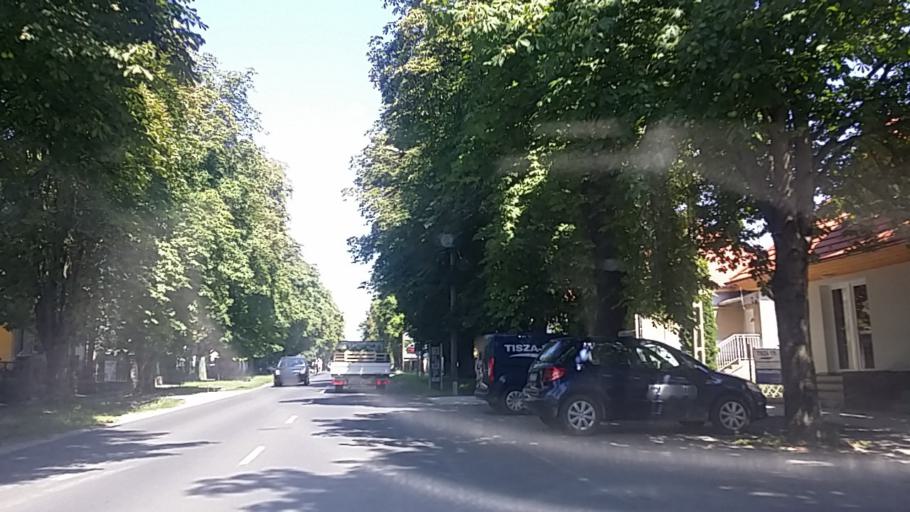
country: HU
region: Zala
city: Keszthely
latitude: 46.7633
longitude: 17.2377
